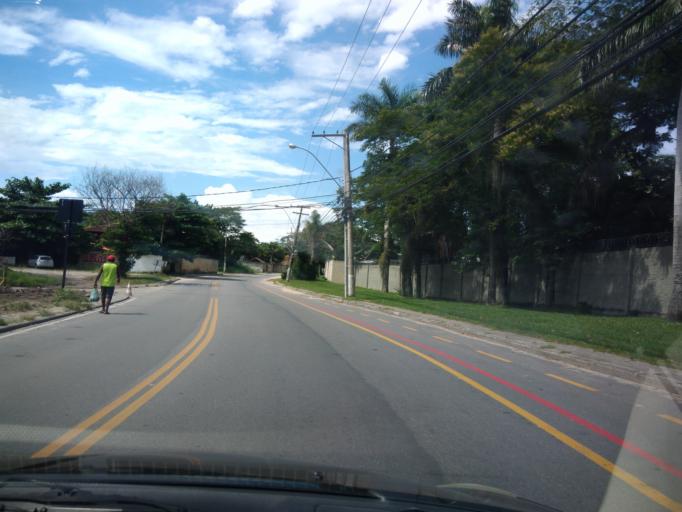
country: BR
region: Rio de Janeiro
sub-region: Niteroi
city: Niteroi
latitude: -22.9450
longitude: -43.0204
